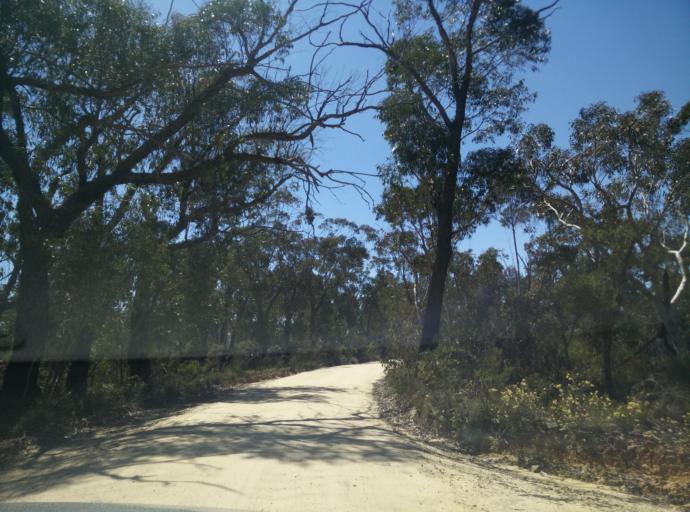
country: AU
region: New South Wales
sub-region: Blue Mountains Municipality
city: Blackheath
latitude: -33.5683
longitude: 150.2807
